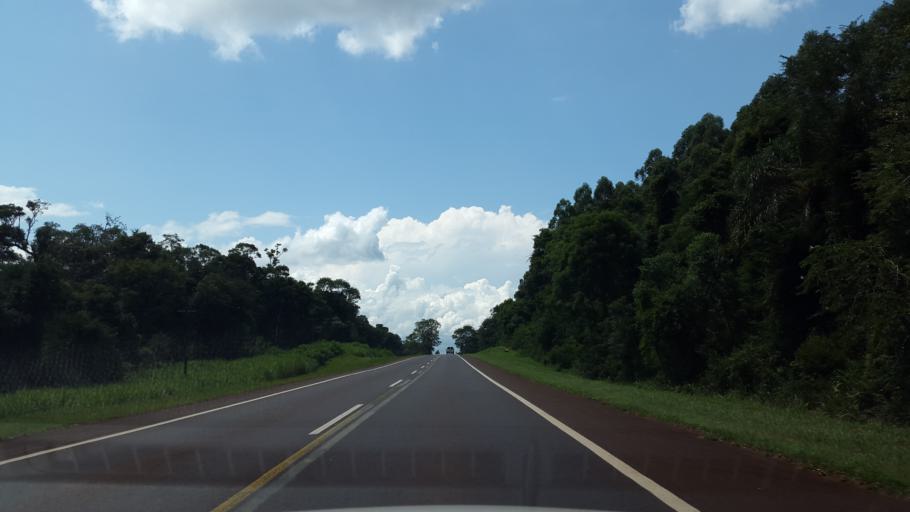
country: AR
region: Misiones
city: El Alcazar
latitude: -26.7059
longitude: -54.8433
